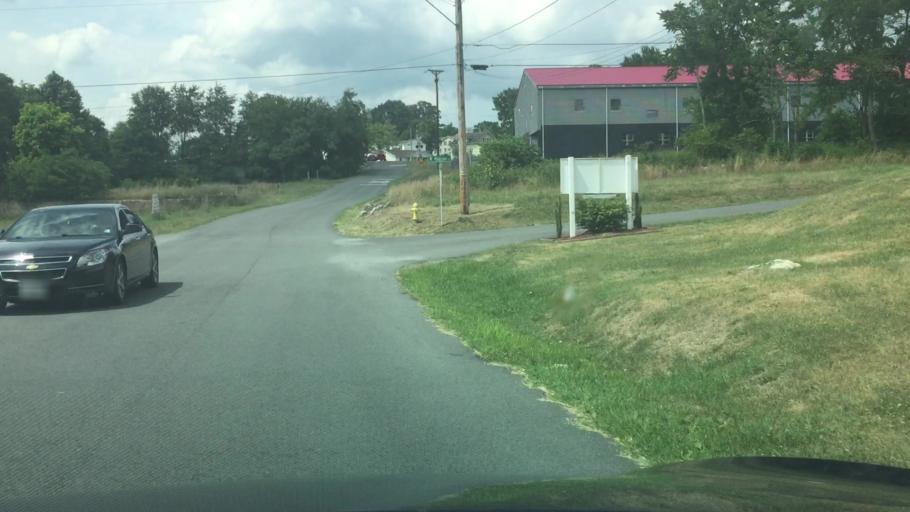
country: US
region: Virginia
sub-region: Wythe County
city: Wytheville
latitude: 36.9404
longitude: -81.0789
